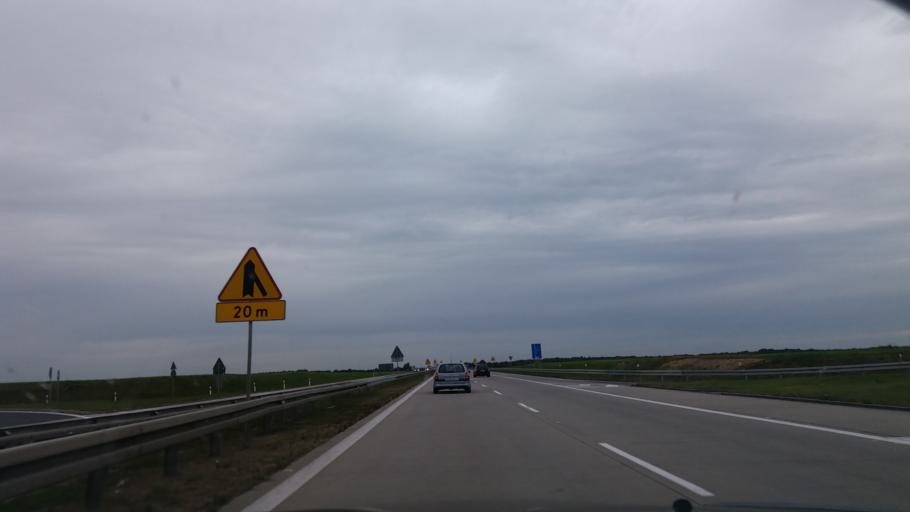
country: PL
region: Lower Silesian Voivodeship
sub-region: Powiat sredzki
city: Udanin
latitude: 51.0706
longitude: 16.4667
